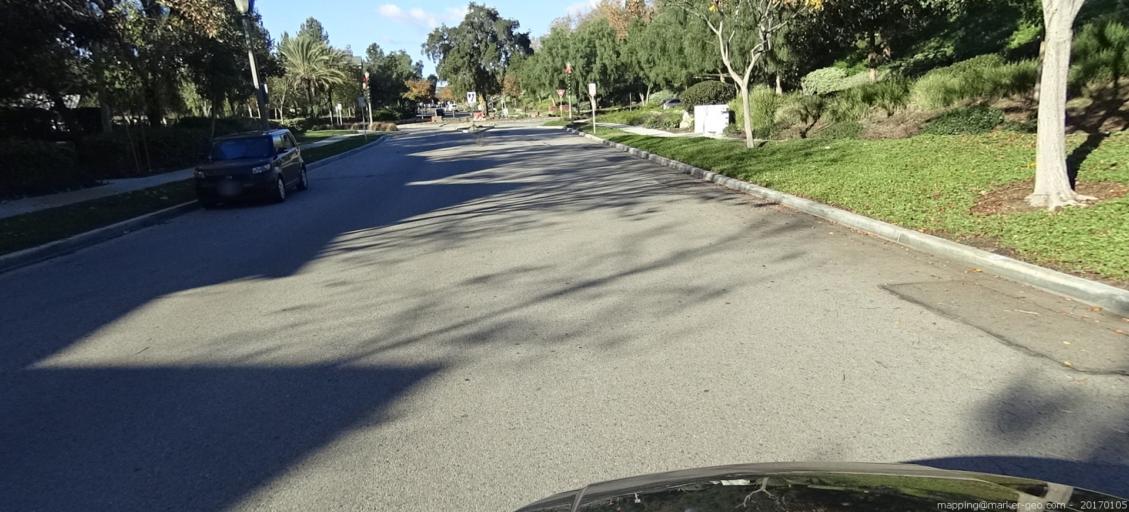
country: US
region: California
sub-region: Orange County
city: Ladera Ranch
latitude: 33.5388
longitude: -117.6435
